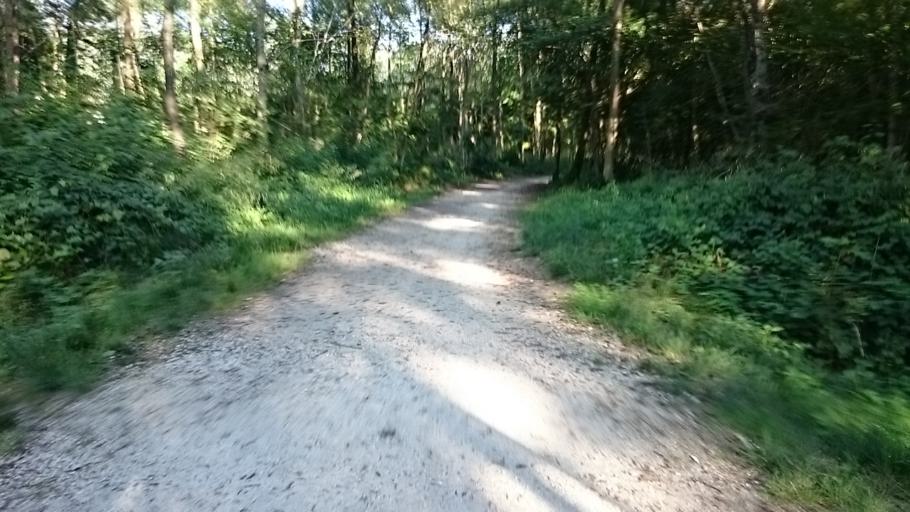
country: IT
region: Veneto
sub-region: Provincia di Belluno
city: Farra d'Alpago
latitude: 46.1238
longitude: 12.3440
